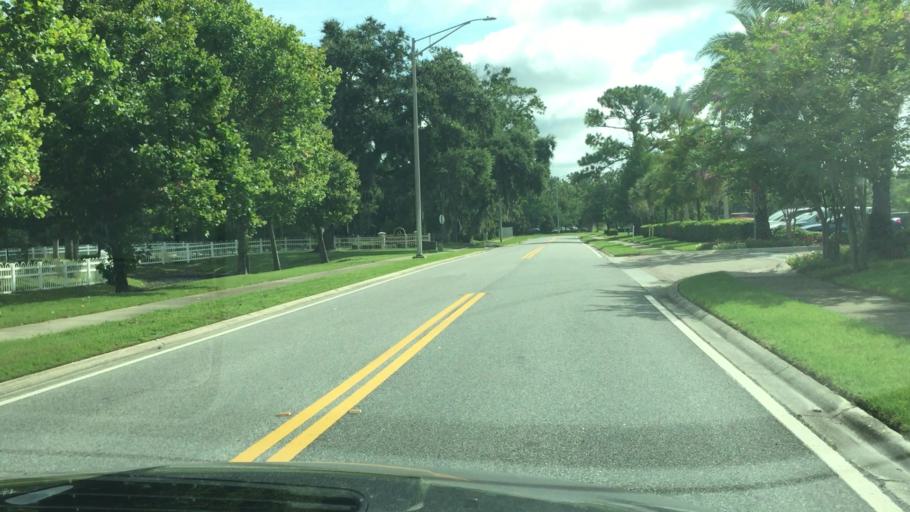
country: US
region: Florida
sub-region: Duval County
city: Jacksonville
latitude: 30.2489
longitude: -81.6001
